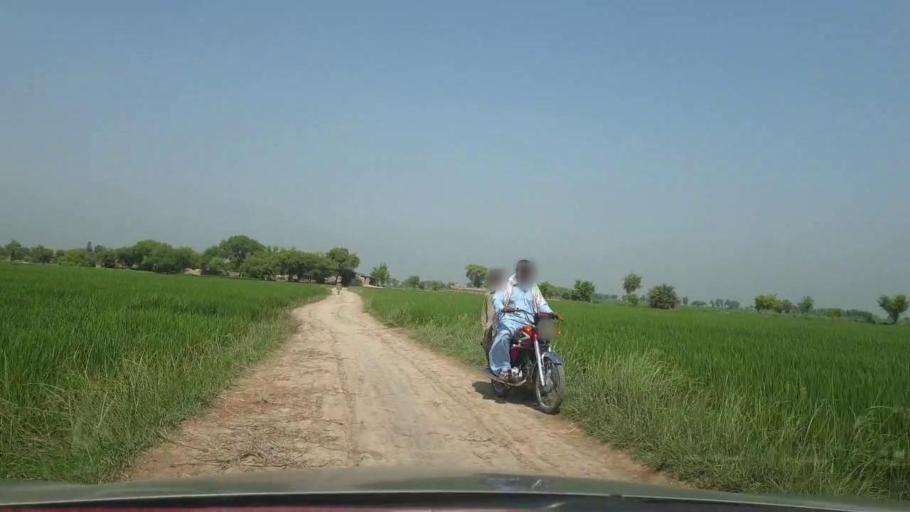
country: PK
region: Sindh
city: Kambar
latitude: 27.5933
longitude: 67.9081
